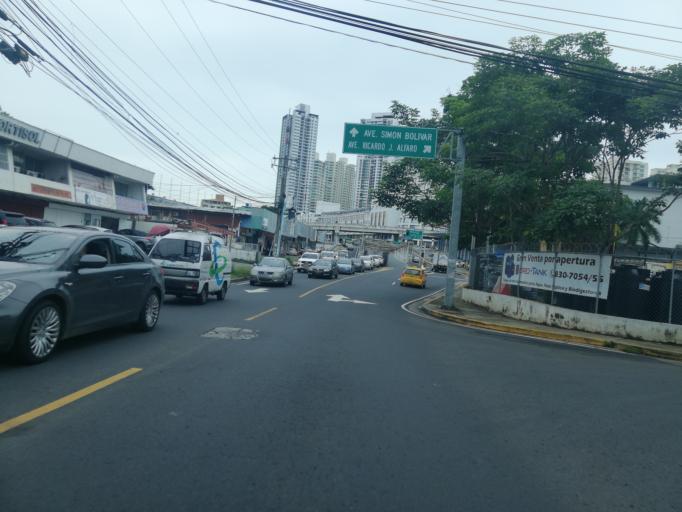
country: PA
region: Panama
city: Panama
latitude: 8.9964
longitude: -79.5354
